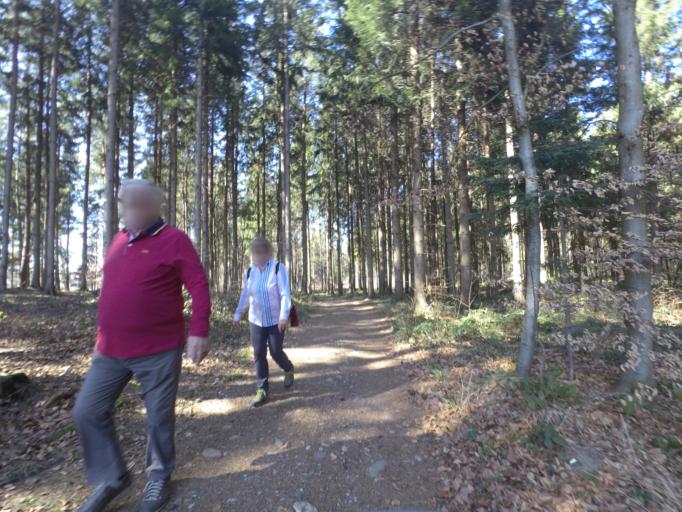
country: AT
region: Salzburg
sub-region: Politischer Bezirk Salzburg-Umgebung
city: Mattsee
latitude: 47.9849
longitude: 13.1018
